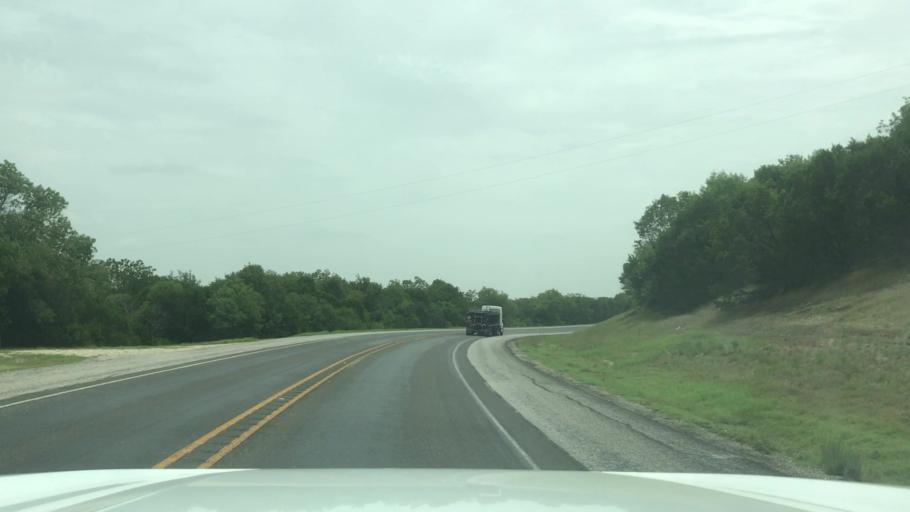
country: US
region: Texas
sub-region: Bosque County
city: Meridian
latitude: 31.8981
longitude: -97.6501
